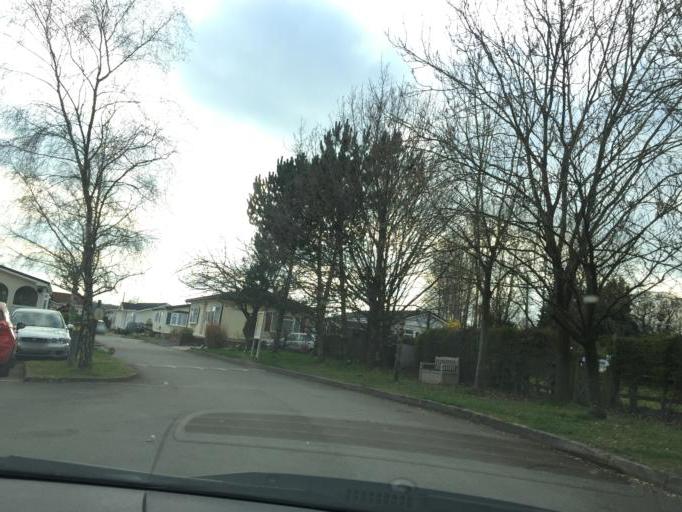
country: GB
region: England
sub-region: Solihull
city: Meriden
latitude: 52.4384
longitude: -1.5908
